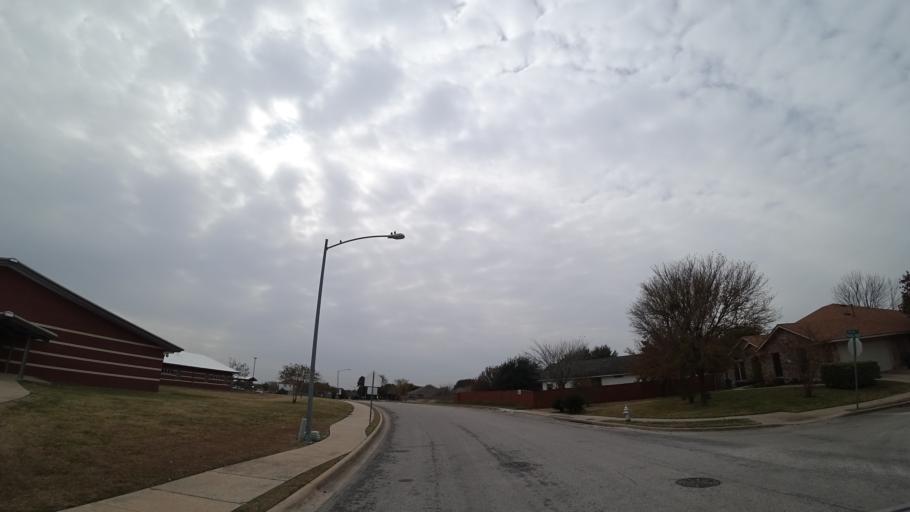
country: US
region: Texas
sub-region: Travis County
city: Garfield
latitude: 30.1579
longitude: -97.6450
